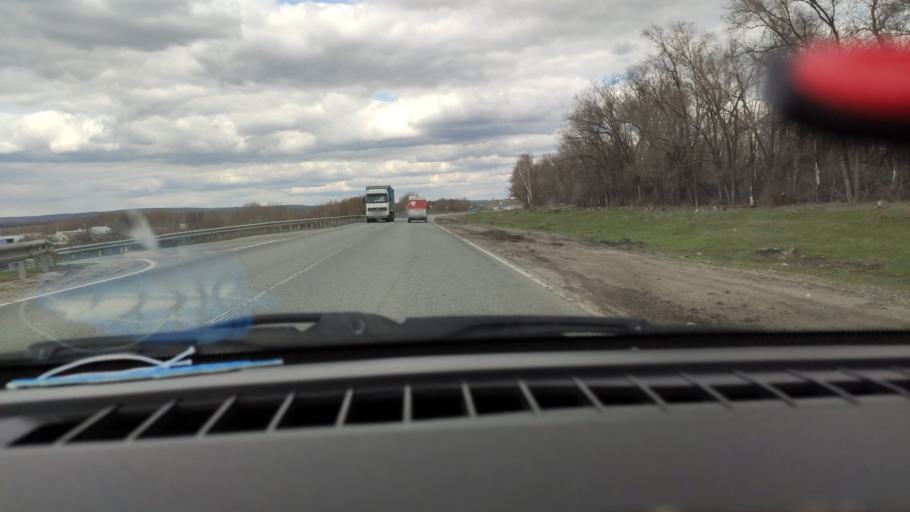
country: RU
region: Saratov
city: Tersa
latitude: 52.0923
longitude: 47.5437
